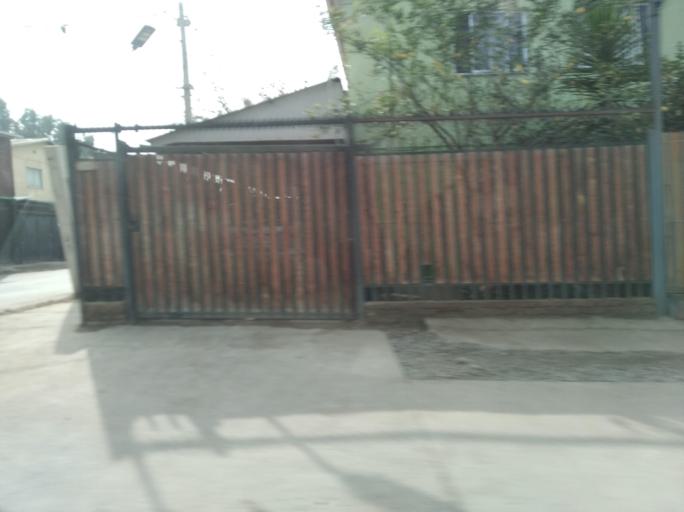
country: CL
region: Santiago Metropolitan
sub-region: Provincia de Chacabuco
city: Lampa
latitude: -33.2873
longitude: -70.8871
